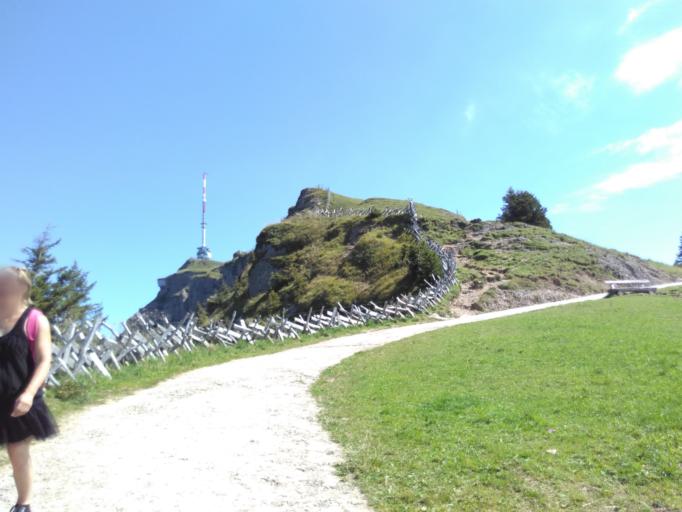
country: CH
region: Lucerne
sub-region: Lucerne-Land District
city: Vitznau
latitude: 47.0550
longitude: 8.4783
